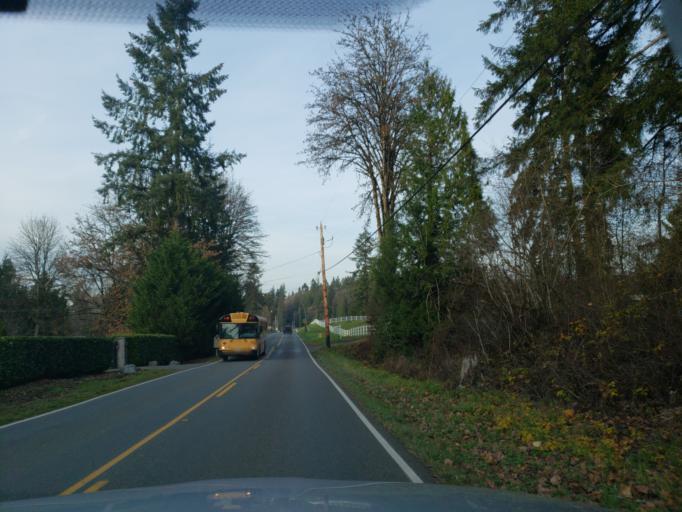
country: US
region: Washington
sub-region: Snohomish County
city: Cathcart
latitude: 47.8325
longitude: -122.0774
